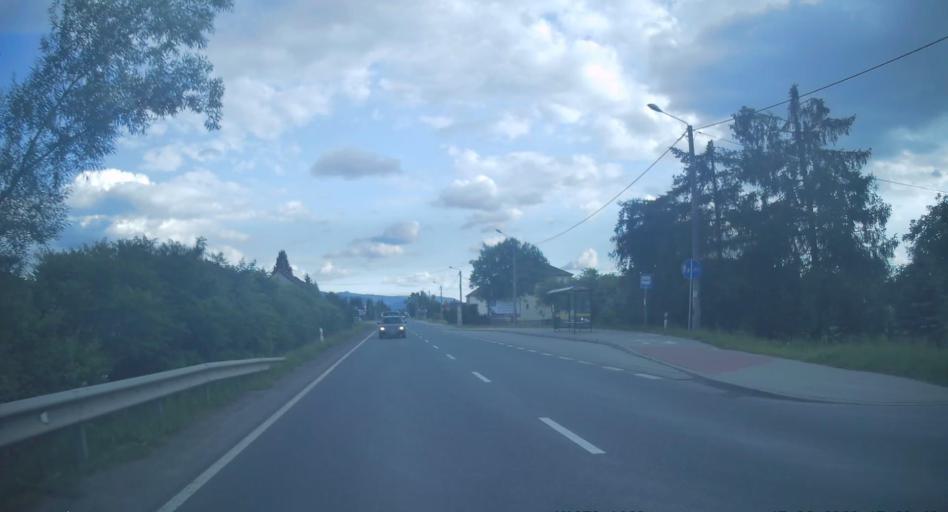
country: PL
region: Lesser Poland Voivodeship
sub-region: Powiat oswiecimski
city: Nowa Wies
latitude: 49.8980
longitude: 19.2181
